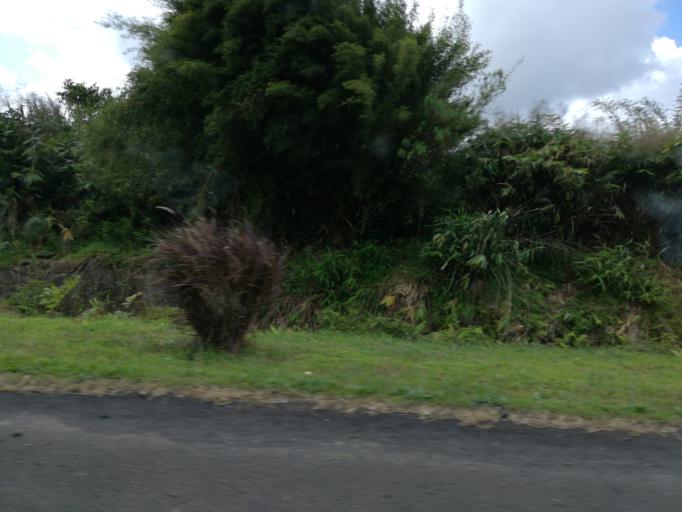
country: MU
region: Plaines Wilhems
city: Midlands
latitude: -20.3403
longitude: 57.5655
